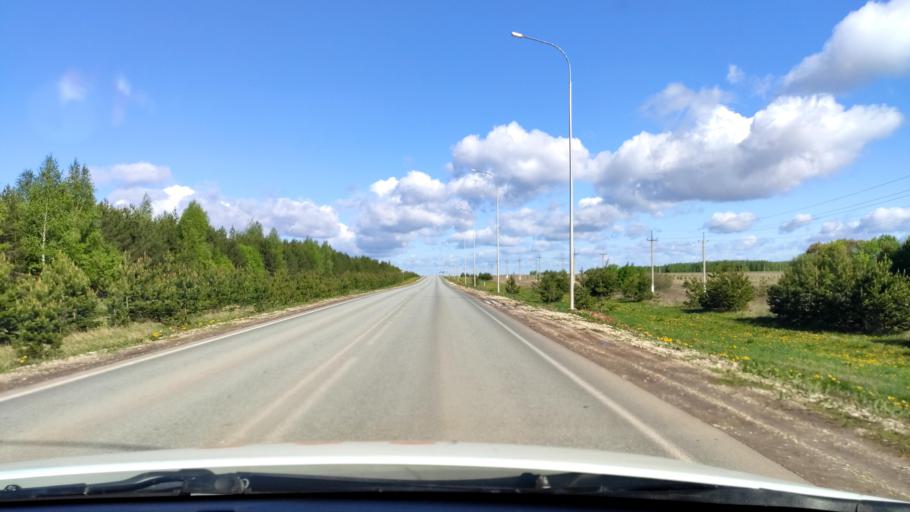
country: RU
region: Tatarstan
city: Sviyazhsk
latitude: 55.7323
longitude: 48.7418
